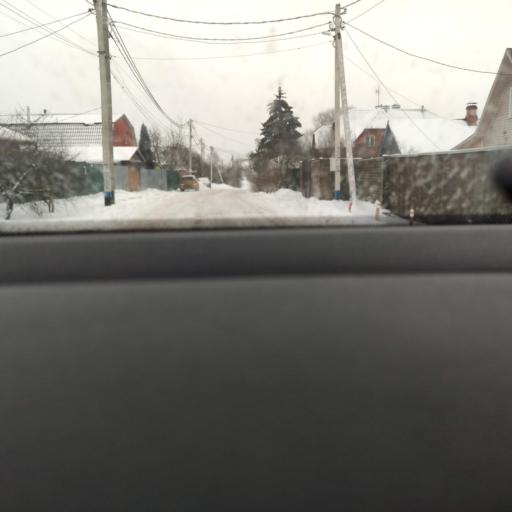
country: RU
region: Moskovskaya
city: Zhukovskiy
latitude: 55.4780
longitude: 38.1487
